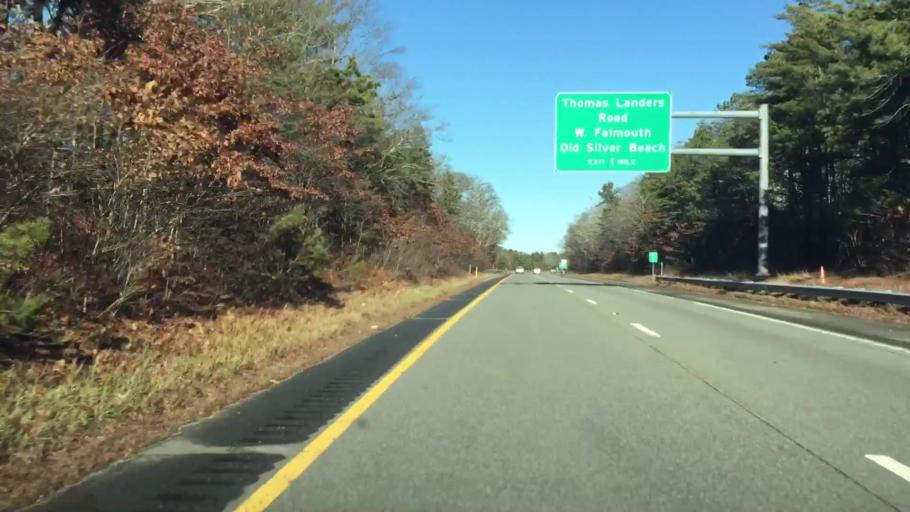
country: US
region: Massachusetts
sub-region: Barnstable County
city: West Falmouth
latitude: 41.6000
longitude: -70.6271
